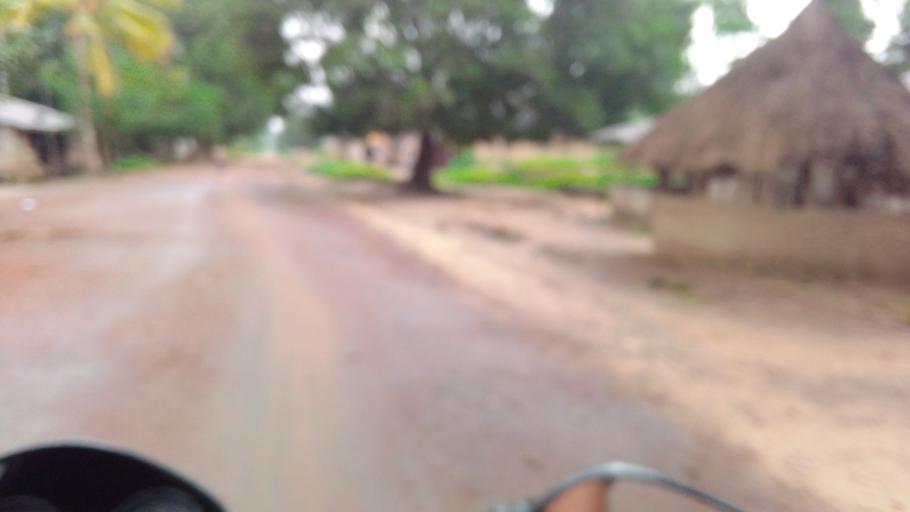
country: SL
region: Northern Province
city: Lunsar
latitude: 8.6898
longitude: -12.5206
